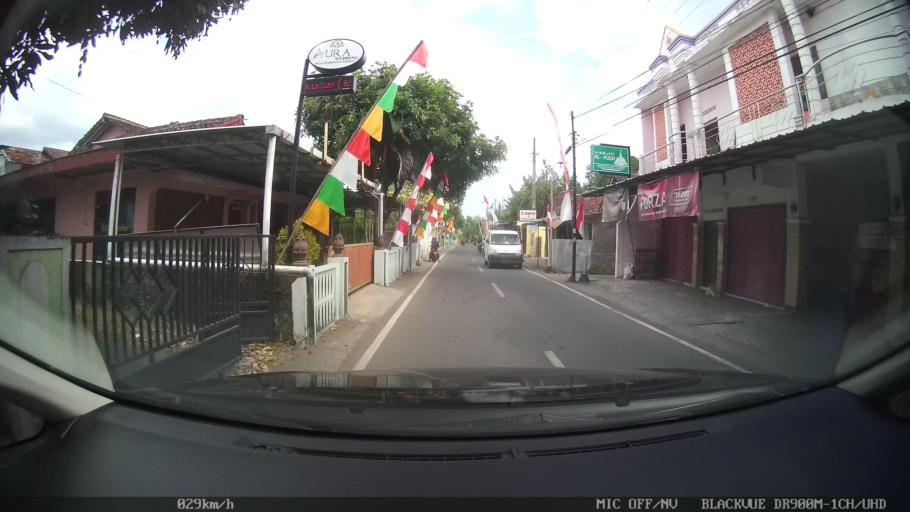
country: ID
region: Daerah Istimewa Yogyakarta
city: Gamping Lor
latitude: -7.8033
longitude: 110.3279
